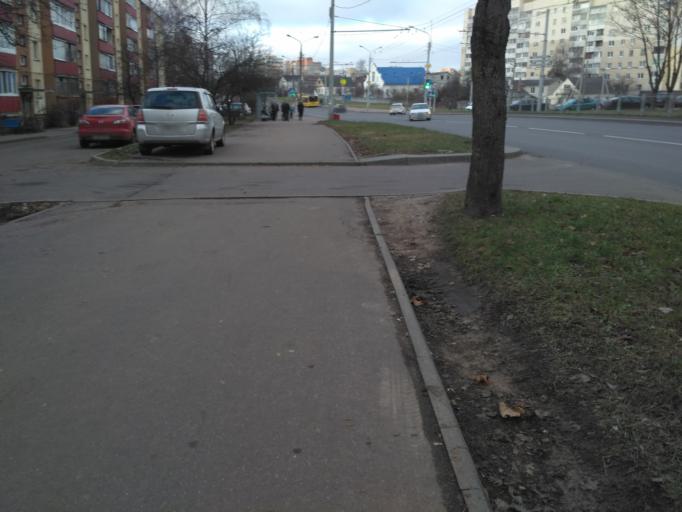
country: BY
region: Minsk
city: Novoye Medvezhino
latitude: 53.9220
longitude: 27.4955
